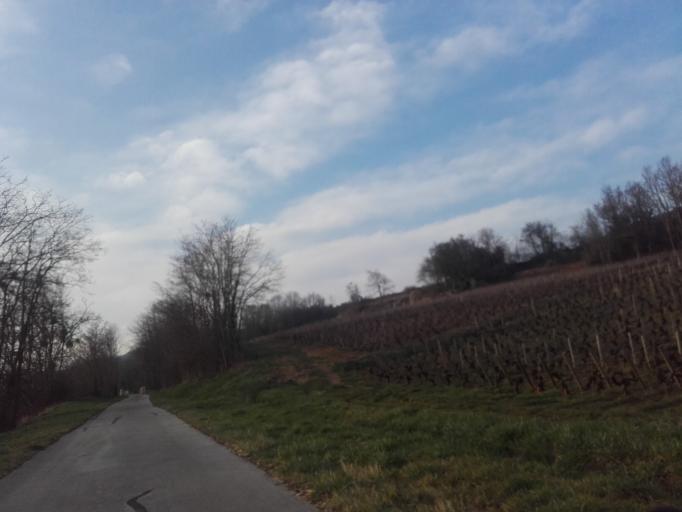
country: FR
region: Bourgogne
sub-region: Departement de la Cote-d'Or
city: Nolay
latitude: 46.9047
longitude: 4.6626
